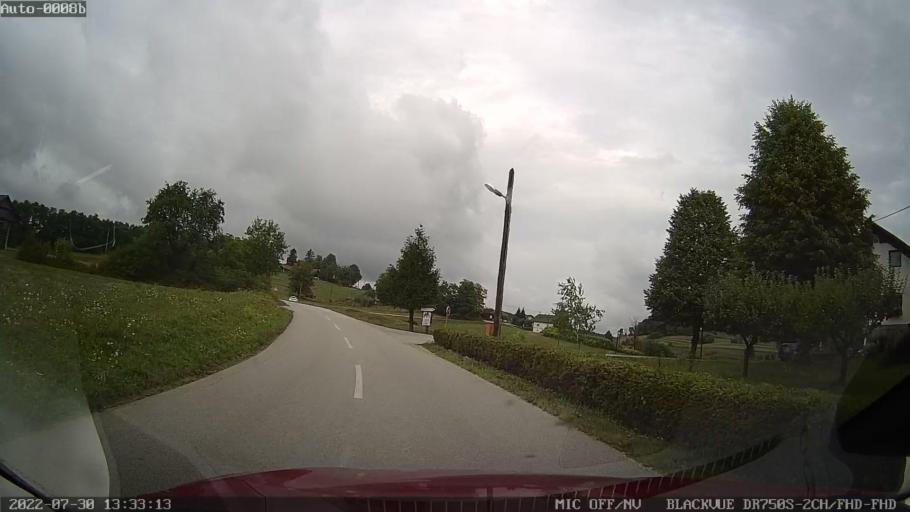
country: SI
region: Zuzemberk
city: Zuzemberk
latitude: 45.8499
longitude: 14.9361
